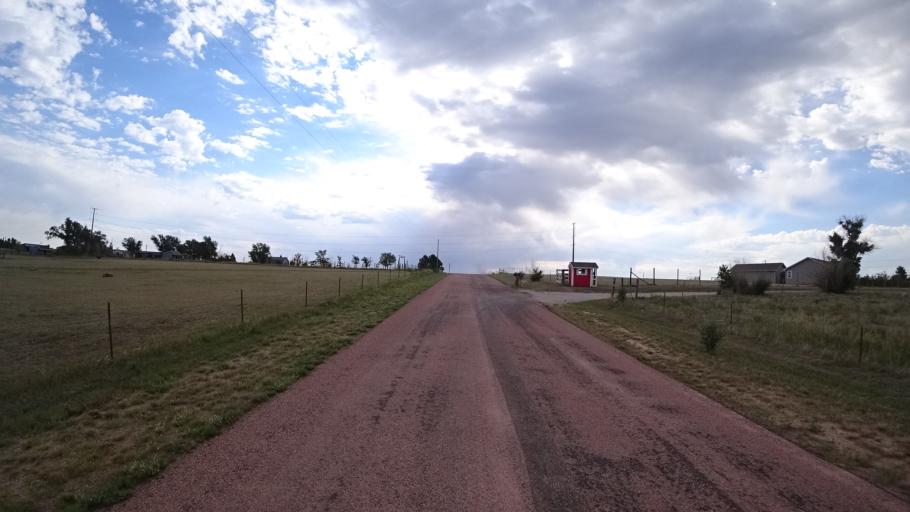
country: US
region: Colorado
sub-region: El Paso County
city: Cimarron Hills
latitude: 38.9155
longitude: -104.6661
